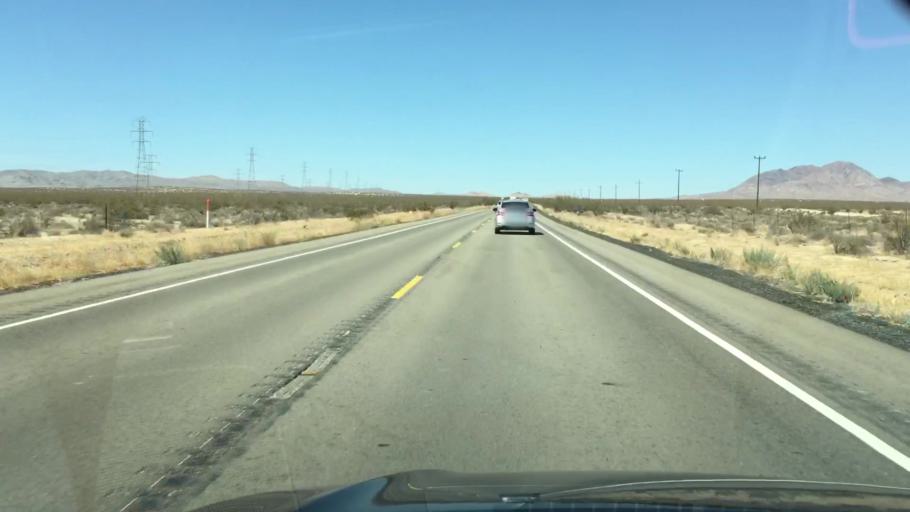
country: US
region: California
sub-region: Kern County
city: Boron
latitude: 35.2422
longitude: -117.6102
